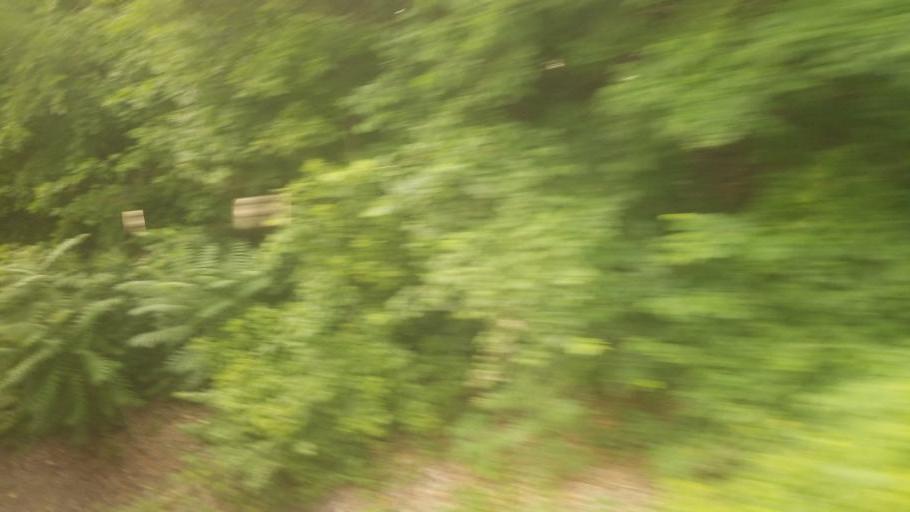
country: US
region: Missouri
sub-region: Jackson County
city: Sugar Creek
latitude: 39.1211
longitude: -94.4565
